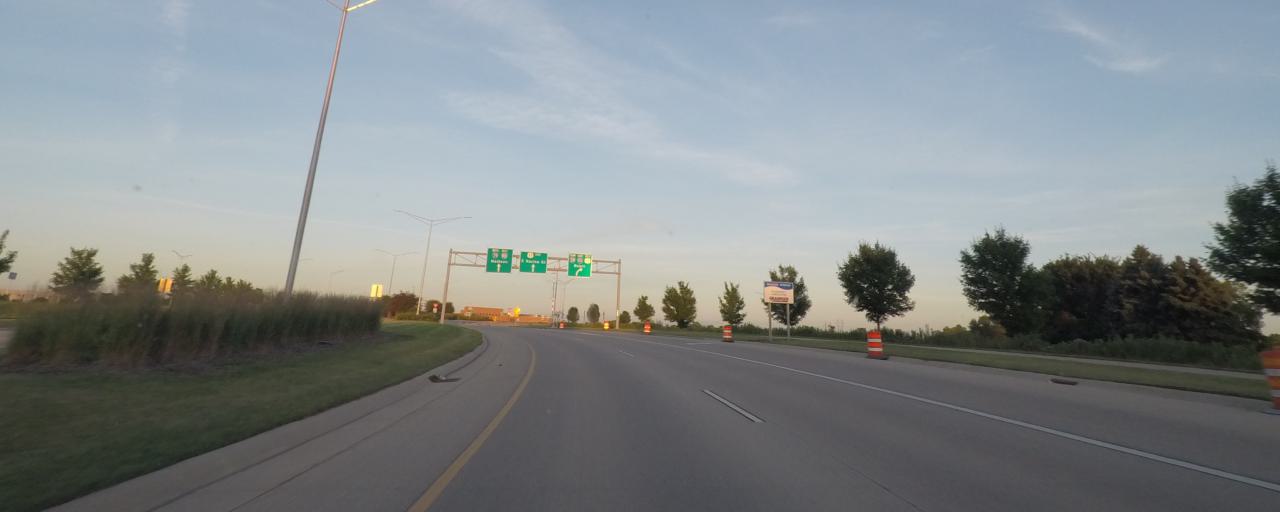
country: US
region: Wisconsin
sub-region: Rock County
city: Janesville
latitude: 42.6714
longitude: -88.9872
